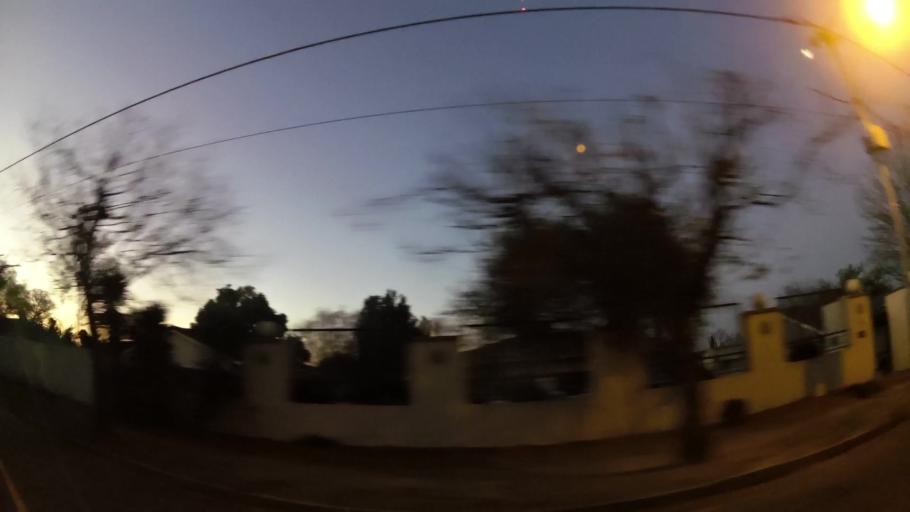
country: ZA
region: Gauteng
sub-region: City of Johannesburg Metropolitan Municipality
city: Roodepoort
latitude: -26.1864
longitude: 27.9251
